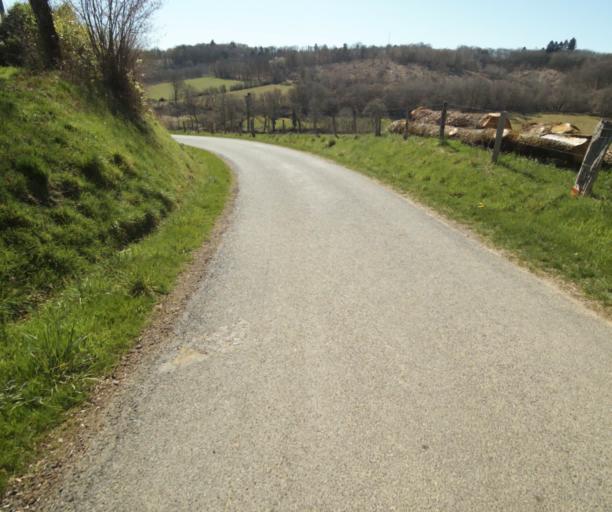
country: FR
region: Limousin
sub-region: Departement de la Correze
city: Chamboulive
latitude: 45.4457
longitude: 1.6945
